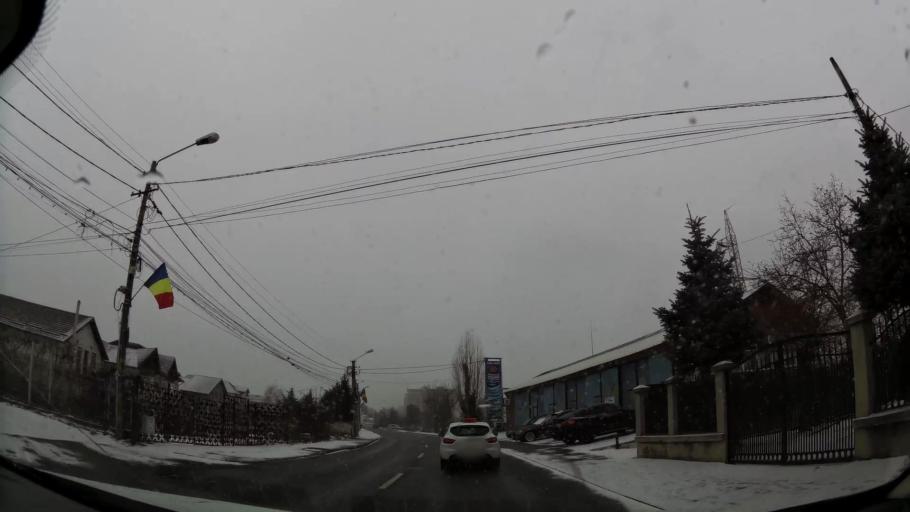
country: RO
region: Dambovita
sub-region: Municipiul Targoviste
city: Targoviste
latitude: 44.9305
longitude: 25.4712
